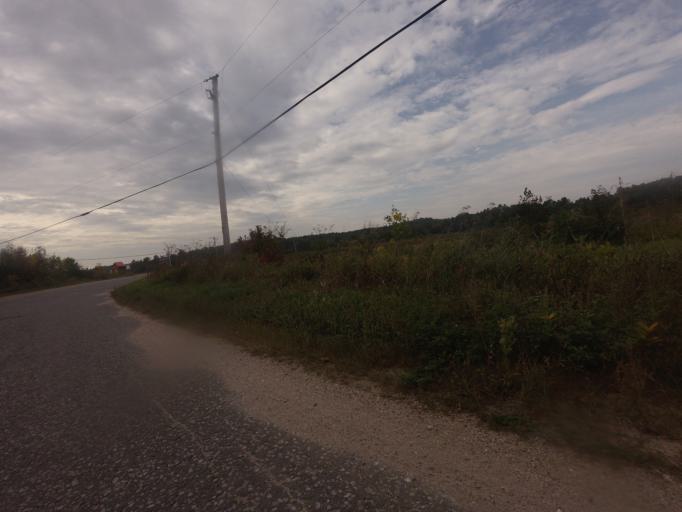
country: CA
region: Quebec
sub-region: Outaouais
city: Wakefield
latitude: 45.9775
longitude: -75.9336
